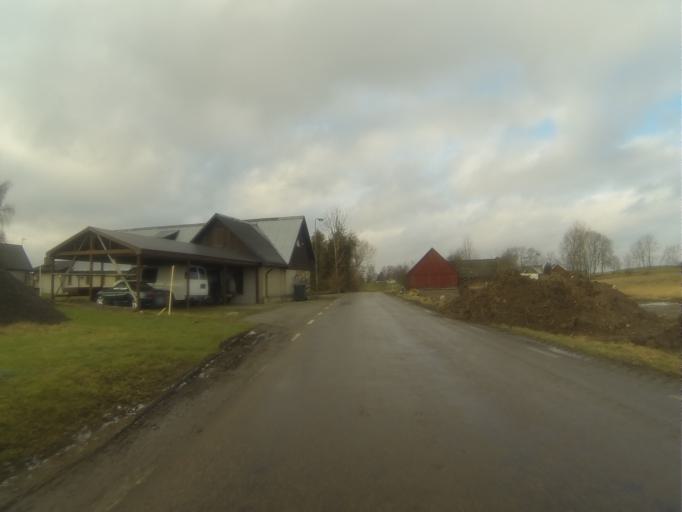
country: SE
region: Skane
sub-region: Svedala Kommun
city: Klagerup
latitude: 55.5698
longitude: 13.3057
